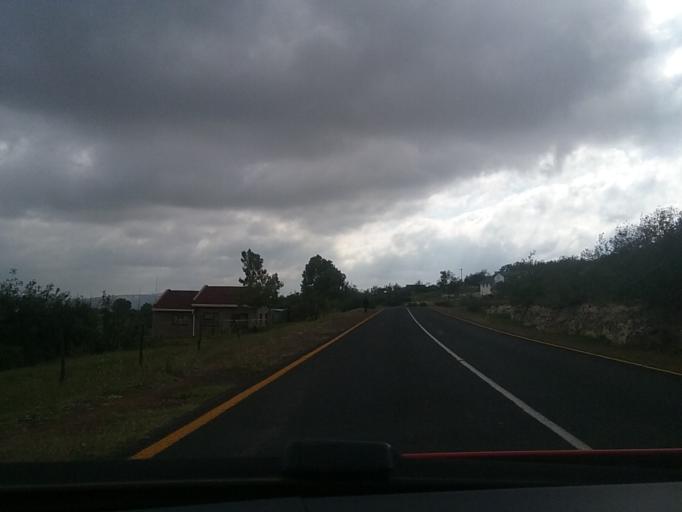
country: LS
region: Berea
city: Teyateyaneng
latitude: -29.1832
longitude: 27.7934
